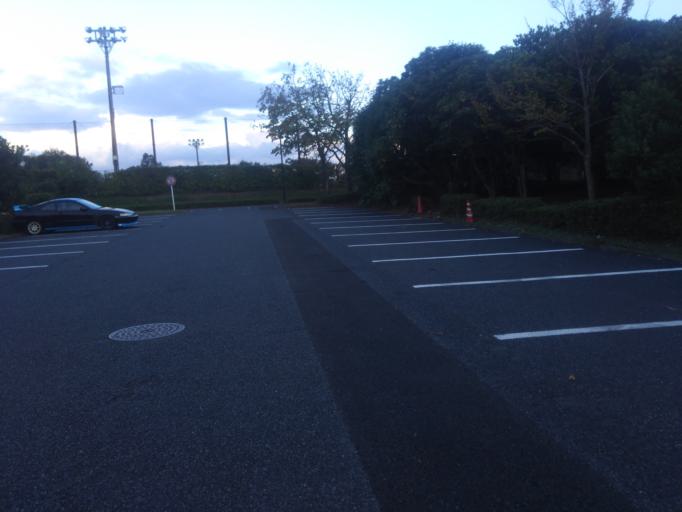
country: JP
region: Tokyo
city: Hino
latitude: 35.6224
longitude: 139.3859
